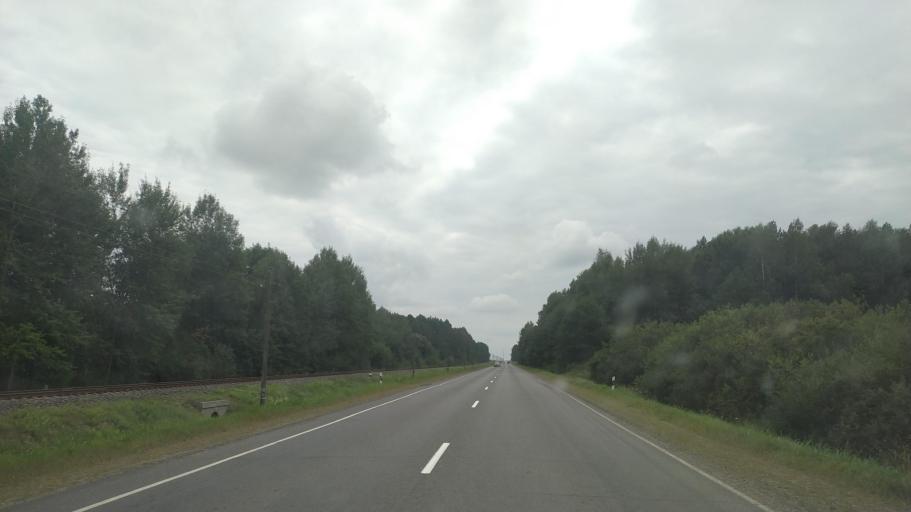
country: BY
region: Brest
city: Byelaazyorsk
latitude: 52.5311
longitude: 25.1439
